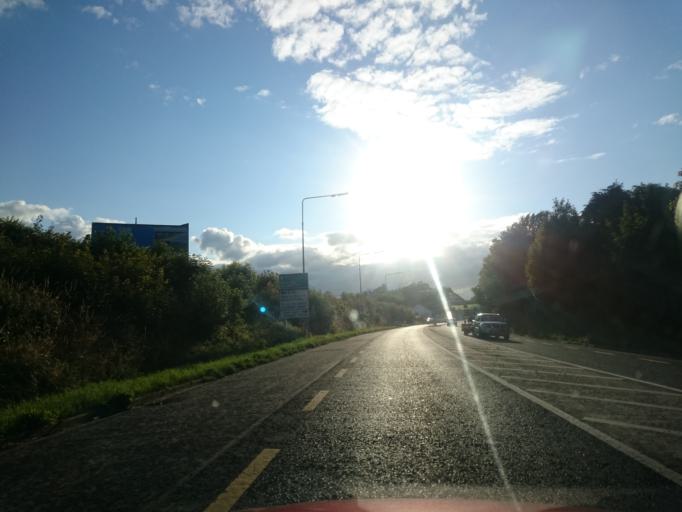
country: IE
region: Leinster
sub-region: Loch Garman
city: Ballygerry
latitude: 52.2430
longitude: -6.3880
